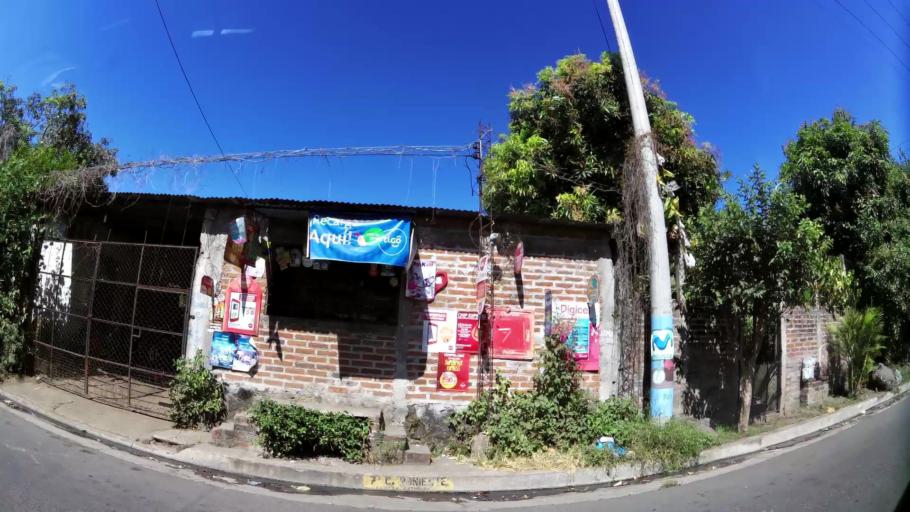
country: SV
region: La Libertad
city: Santa Tecla
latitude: 13.7344
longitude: -89.3815
